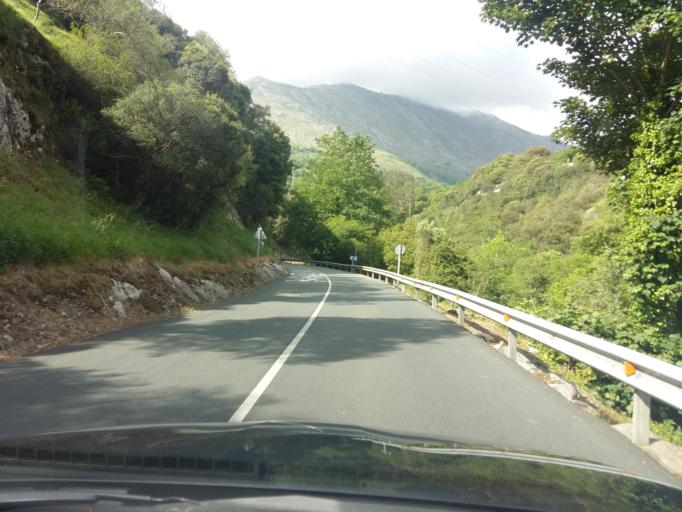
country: ES
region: Cantabria
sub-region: Provincia de Cantabria
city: Tresviso
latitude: 43.3204
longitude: -4.6053
